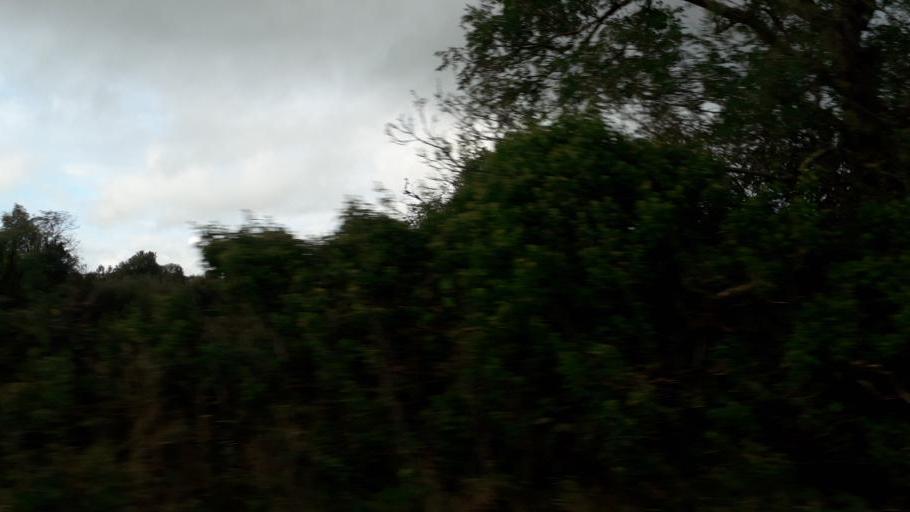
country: IE
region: Leinster
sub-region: An Longfort
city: Lanesborough
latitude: 53.7665
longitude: -8.0871
